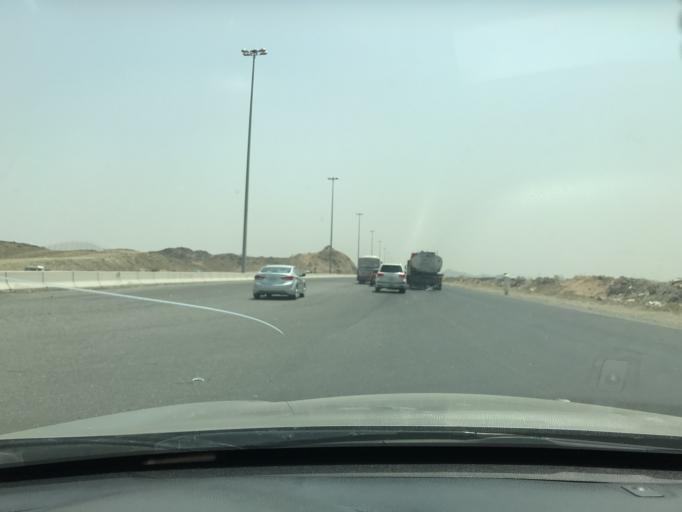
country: SA
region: Makkah
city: Jeddah
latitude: 21.6154
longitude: 39.2538
